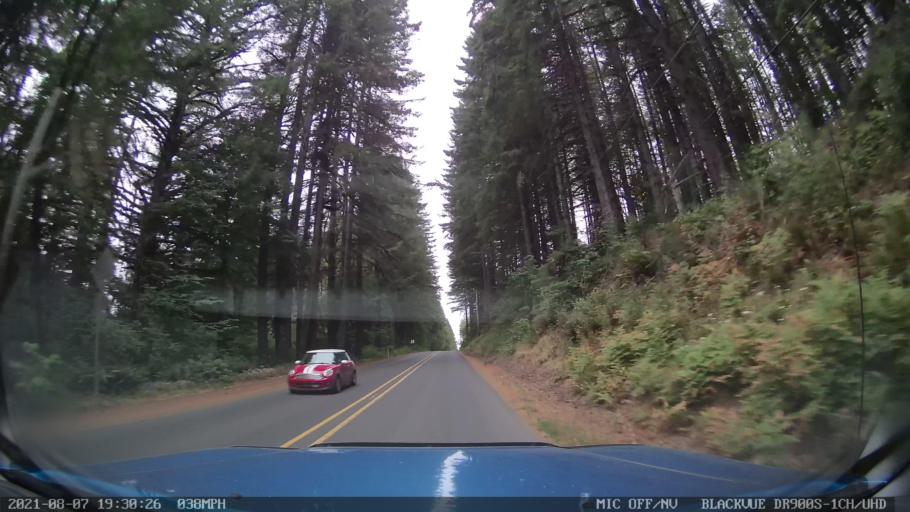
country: US
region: Oregon
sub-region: Linn County
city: Lyons
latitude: 44.8849
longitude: -122.6207
